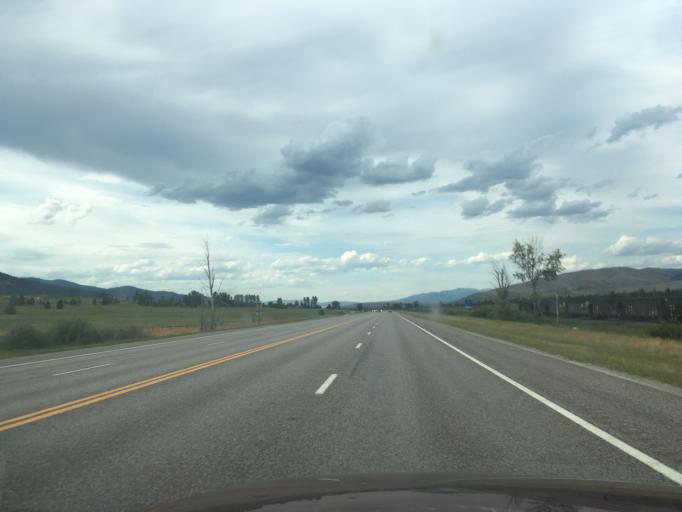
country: US
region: Montana
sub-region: Missoula County
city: Lolo
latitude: 46.6900
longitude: -114.0740
